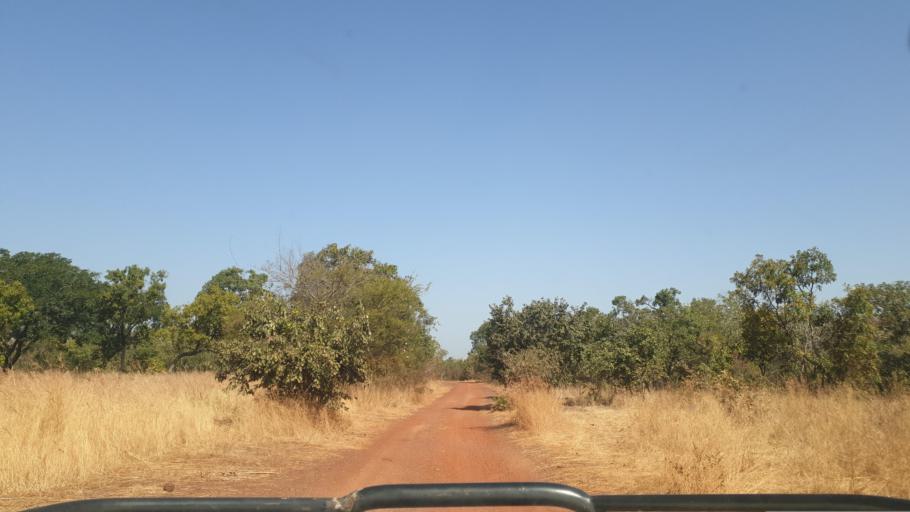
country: ML
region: Koulikoro
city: Dioila
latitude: 11.9144
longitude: -6.9847
